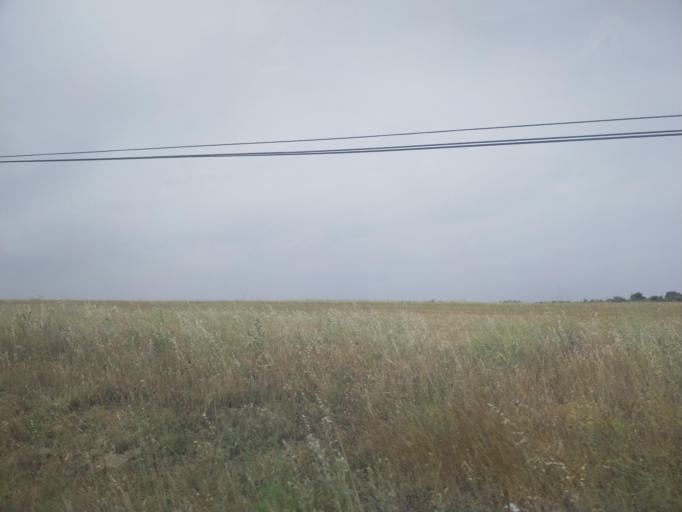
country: ES
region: Castille-La Mancha
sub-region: Province of Toledo
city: Casasbuenas
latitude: 39.7637
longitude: -4.1360
